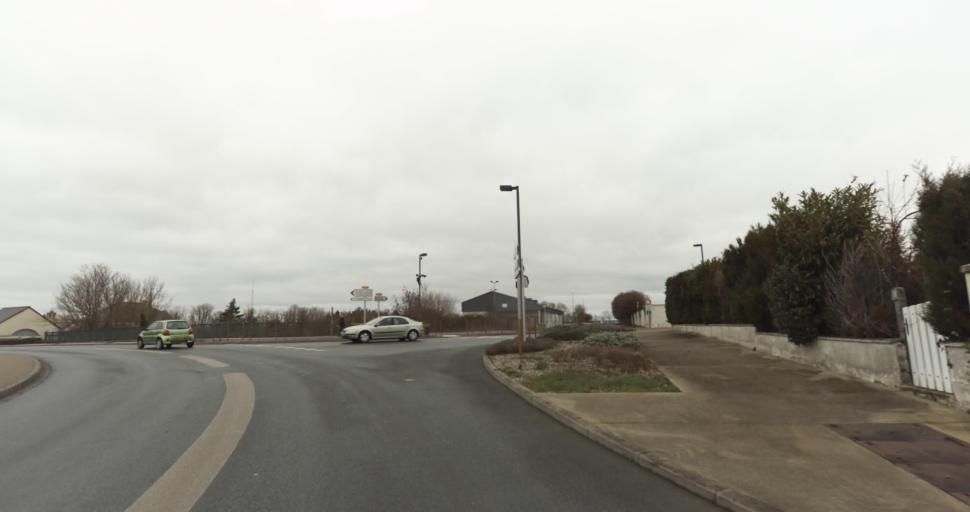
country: FR
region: Pays de la Loire
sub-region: Departement de Maine-et-Loire
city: Montreuil-Bellay
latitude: 47.1297
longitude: -0.1497
